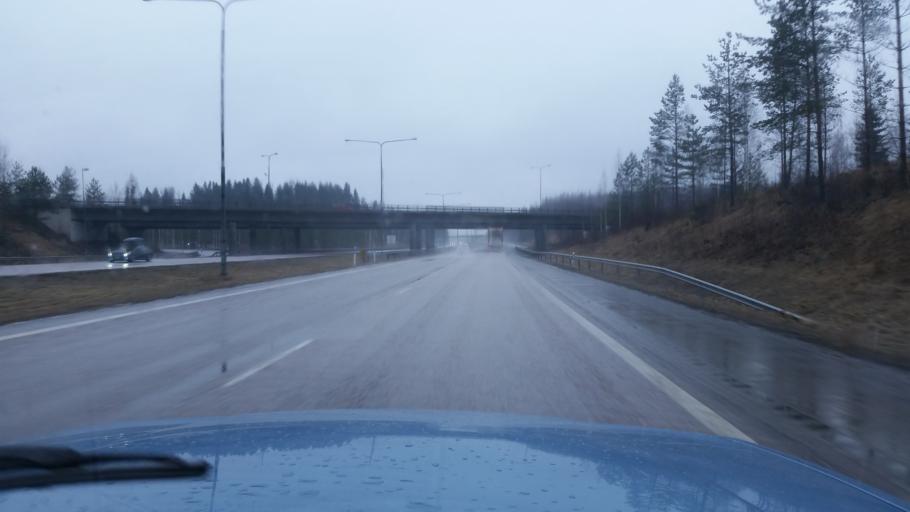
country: FI
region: Uusimaa
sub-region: Helsinki
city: Hyvinge
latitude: 60.5649
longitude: 24.8204
